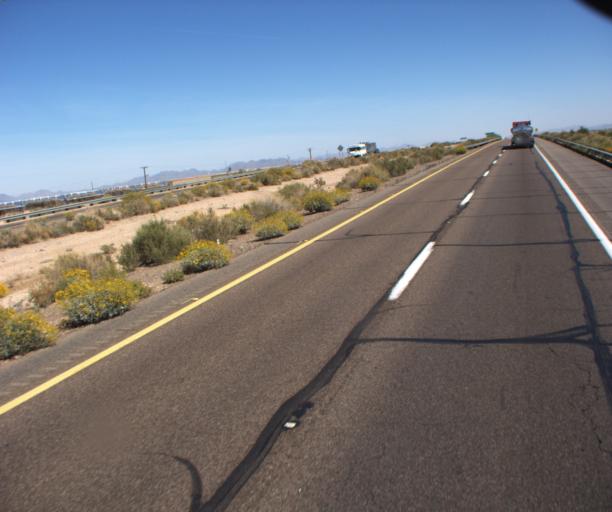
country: US
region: Arizona
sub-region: Maricopa County
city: Gila Bend
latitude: 32.9109
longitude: -112.9621
